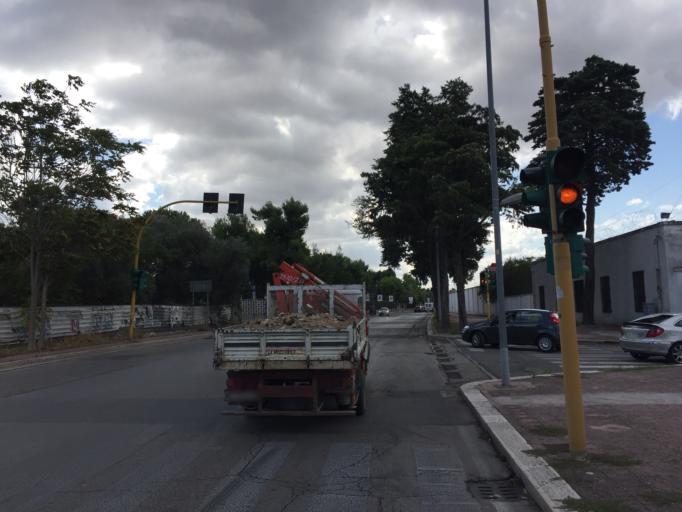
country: IT
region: Apulia
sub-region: Provincia di Bari
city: Bari
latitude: 41.0954
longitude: 16.8828
